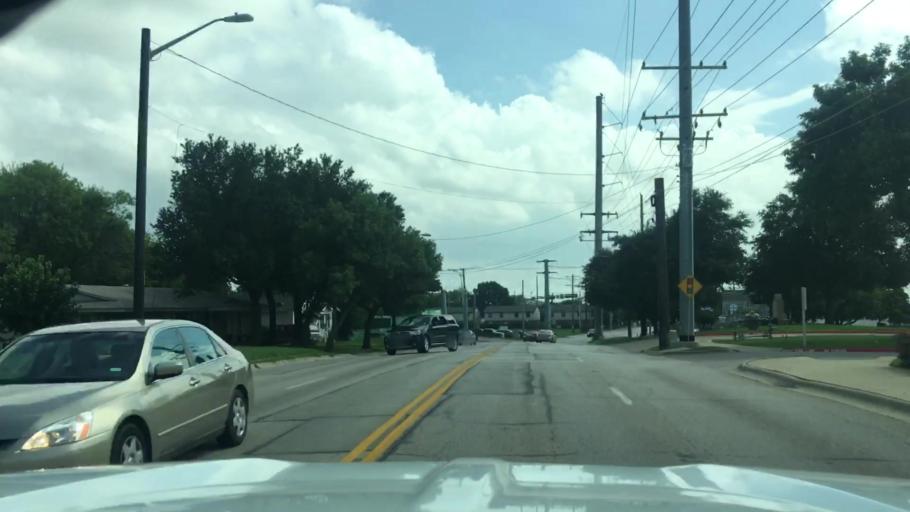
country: US
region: Texas
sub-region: Denton County
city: Denton
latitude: 33.2171
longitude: -97.1616
